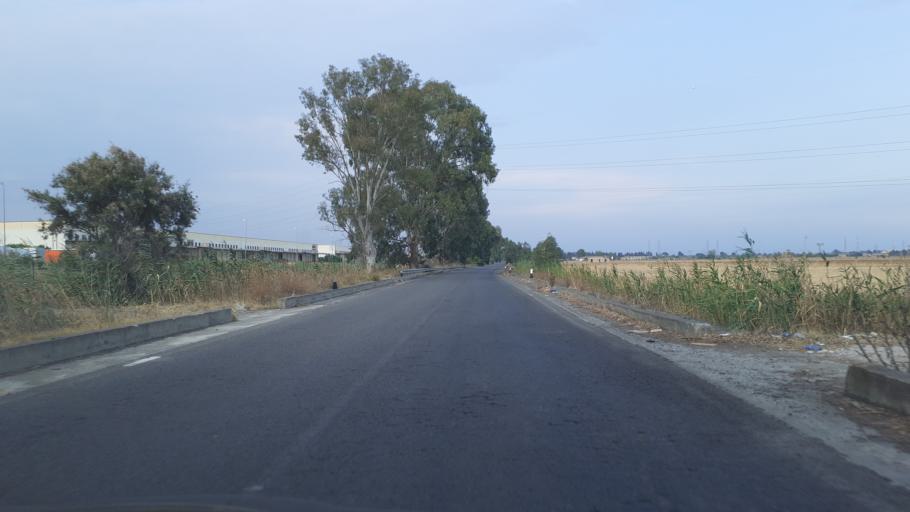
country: IT
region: Sicily
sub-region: Catania
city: Misterbianco
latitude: 37.4417
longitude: 15.0109
